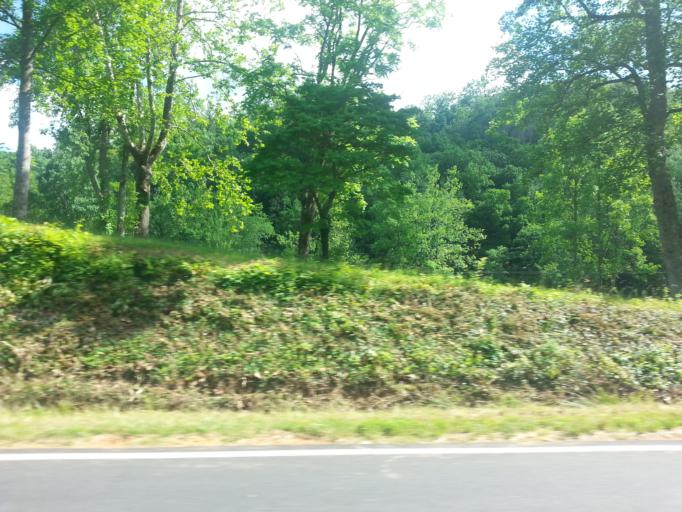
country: US
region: Georgia
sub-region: Towns County
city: Hiawassee
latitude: 34.8340
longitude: -83.7367
